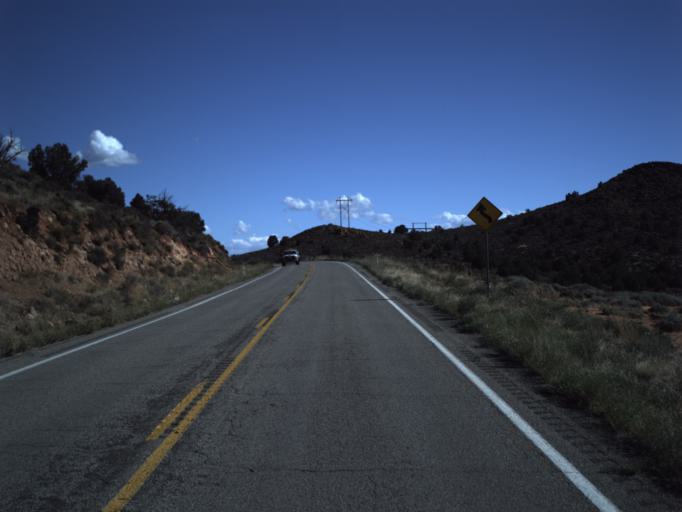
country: US
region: Utah
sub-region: Washington County
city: Toquerville
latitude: 37.2786
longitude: -113.3040
